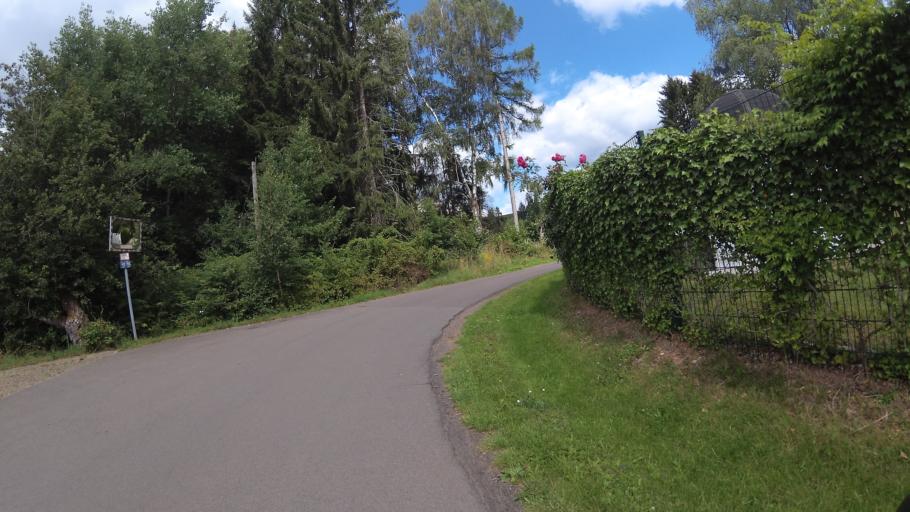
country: DE
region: Saarland
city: Weiskirchen
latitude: 49.5641
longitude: 6.8140
